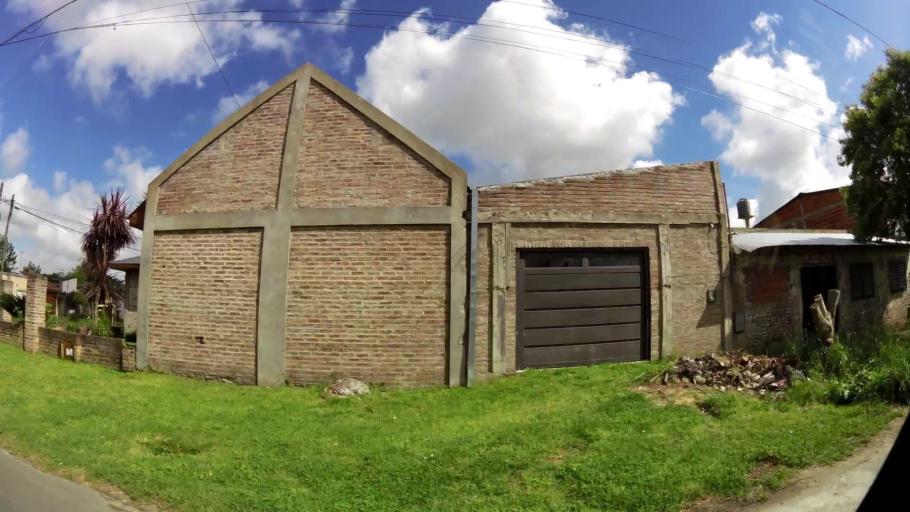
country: AR
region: Buenos Aires
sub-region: Partido de Quilmes
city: Quilmes
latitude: -34.8297
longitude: -58.1712
